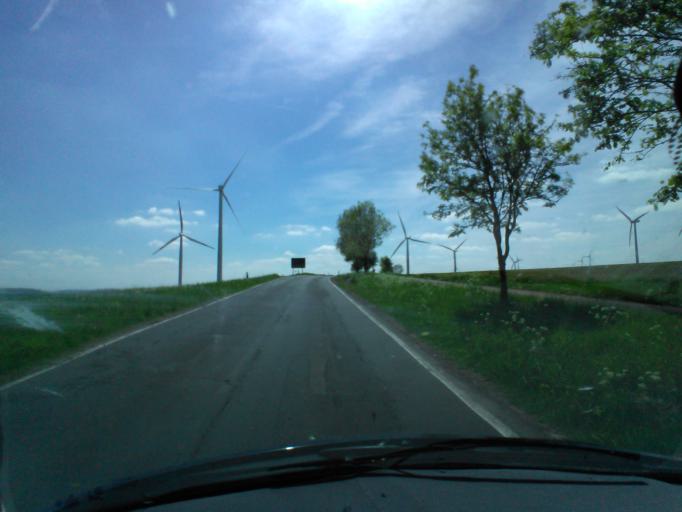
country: DE
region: Rheinland-Pfalz
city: Grosslangenfeld
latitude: 50.1942
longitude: 6.2427
